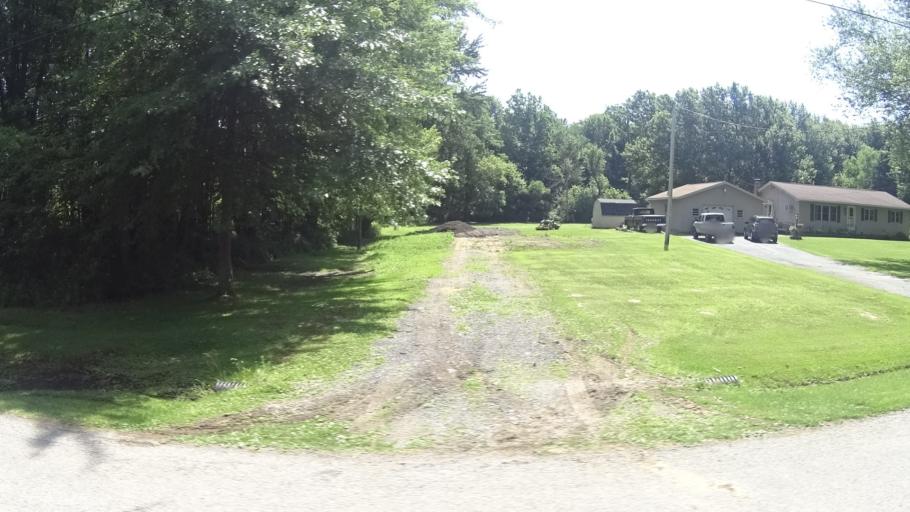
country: US
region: Ohio
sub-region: Huron County
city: Wakeman
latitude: 41.3406
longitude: -82.4591
